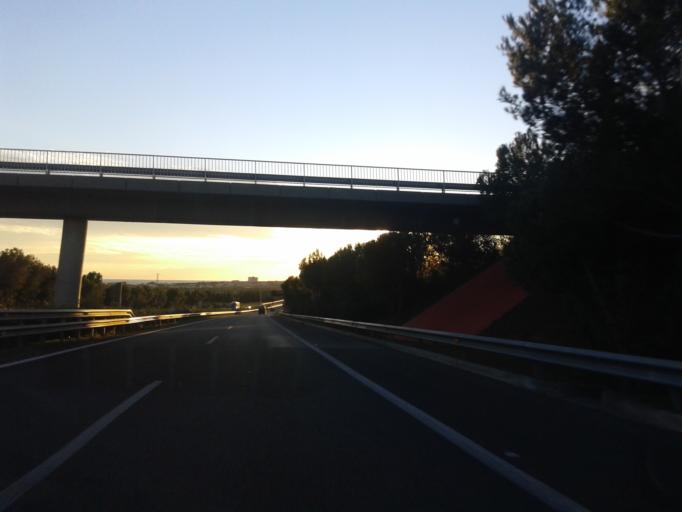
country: ES
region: Catalonia
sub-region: Provincia de Tarragona
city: Calafell
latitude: 41.2005
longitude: 1.5478
